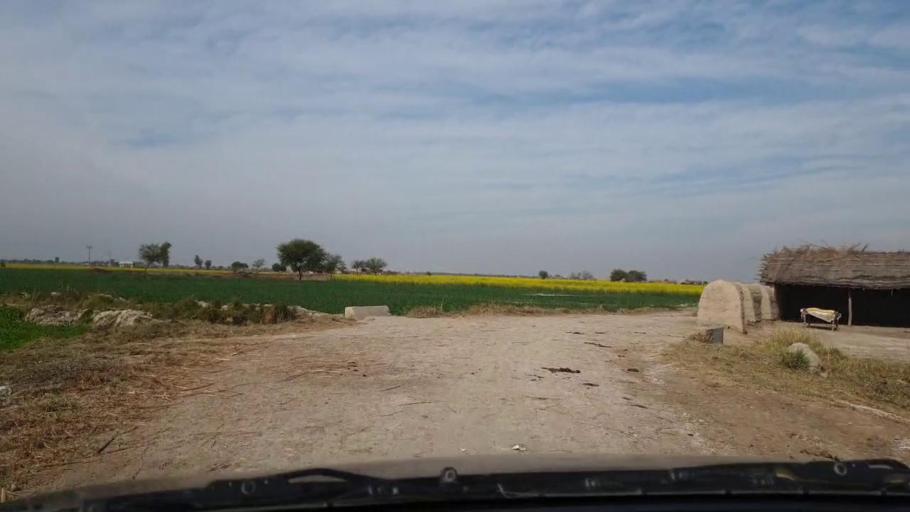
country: PK
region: Sindh
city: Jam Sahib
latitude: 26.2713
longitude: 68.7088
